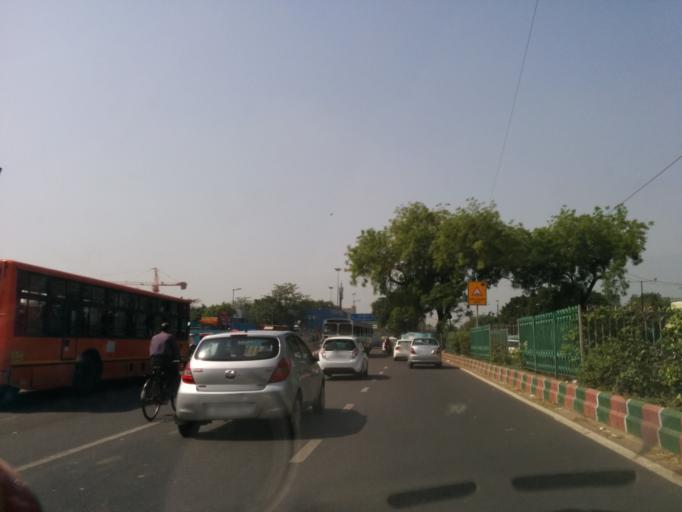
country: IN
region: NCT
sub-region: New Delhi
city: New Delhi
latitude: 28.5742
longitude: 77.2095
